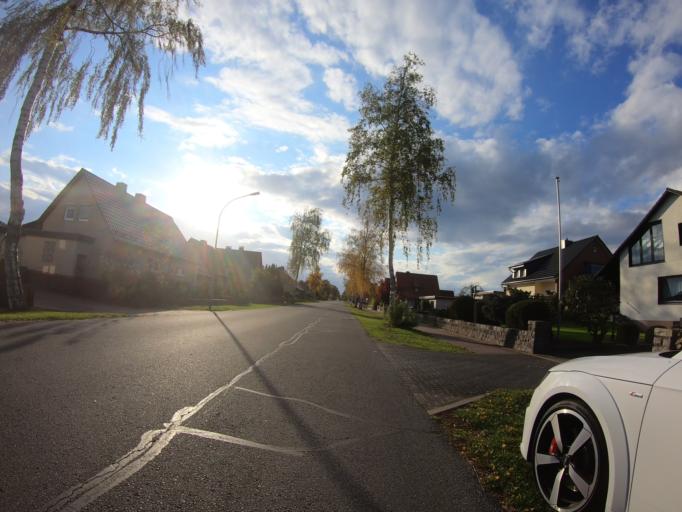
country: DE
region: Lower Saxony
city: Wagenhoff
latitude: 52.5523
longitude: 10.5268
